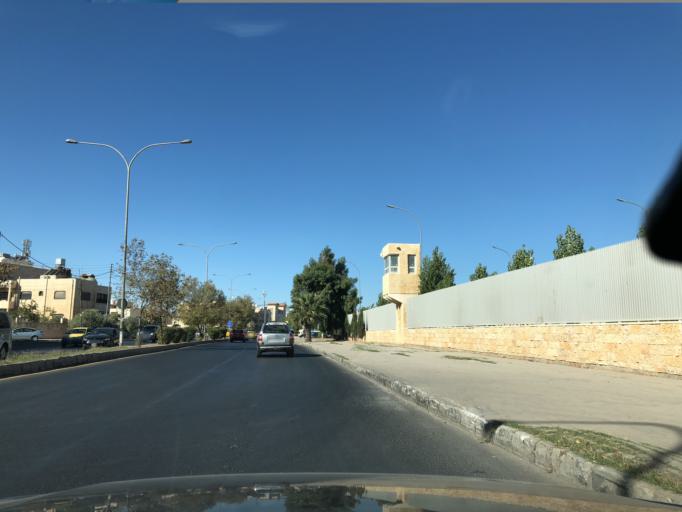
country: JO
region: Amman
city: Wadi as Sir
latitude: 31.9695
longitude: 35.8362
